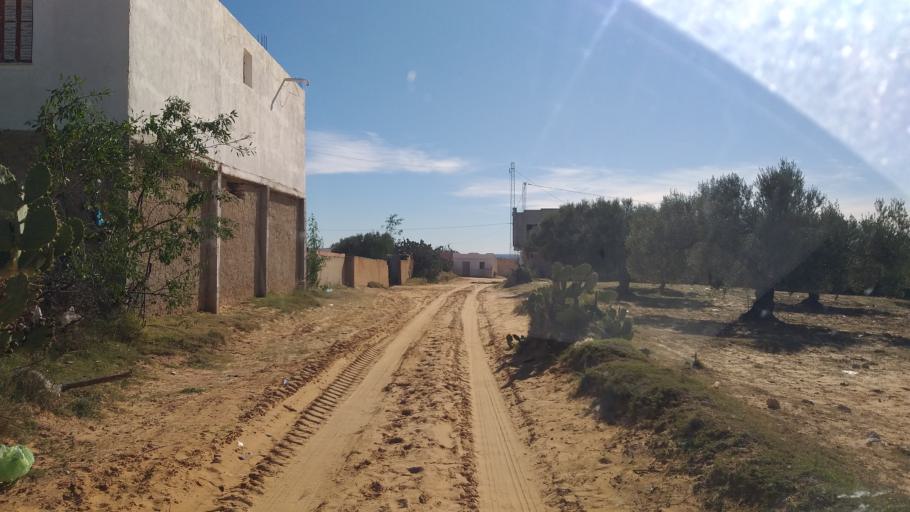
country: TN
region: Al Mahdiyah
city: El Jem
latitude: 35.2551
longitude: 10.6070
